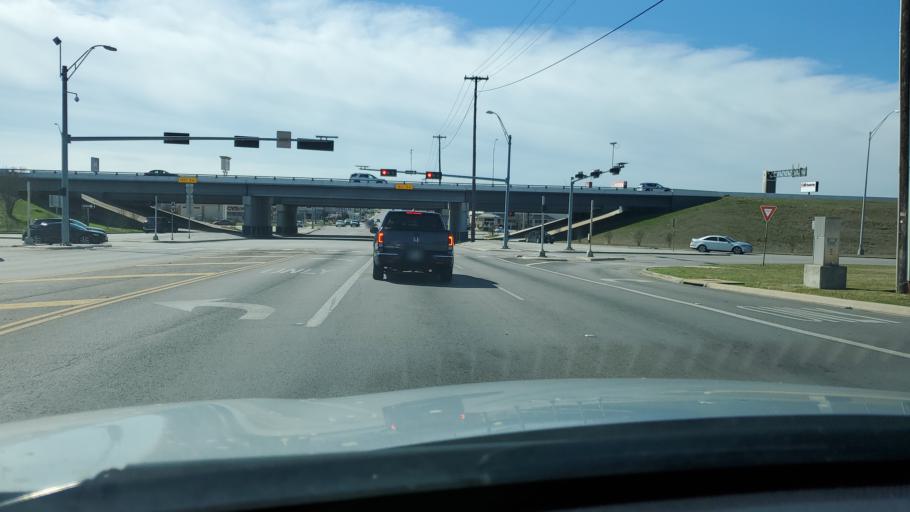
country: US
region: Texas
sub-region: Bell County
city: Killeen
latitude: 31.0956
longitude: -97.7321
